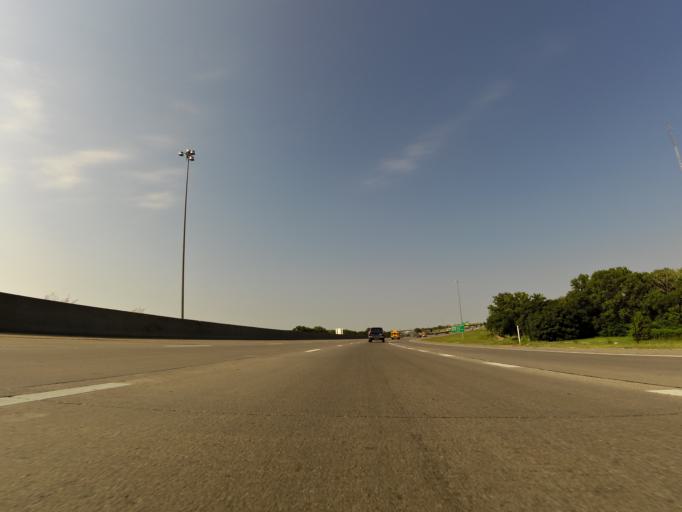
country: US
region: Kansas
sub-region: Sedgwick County
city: Wichita
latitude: 37.7164
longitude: -97.3219
